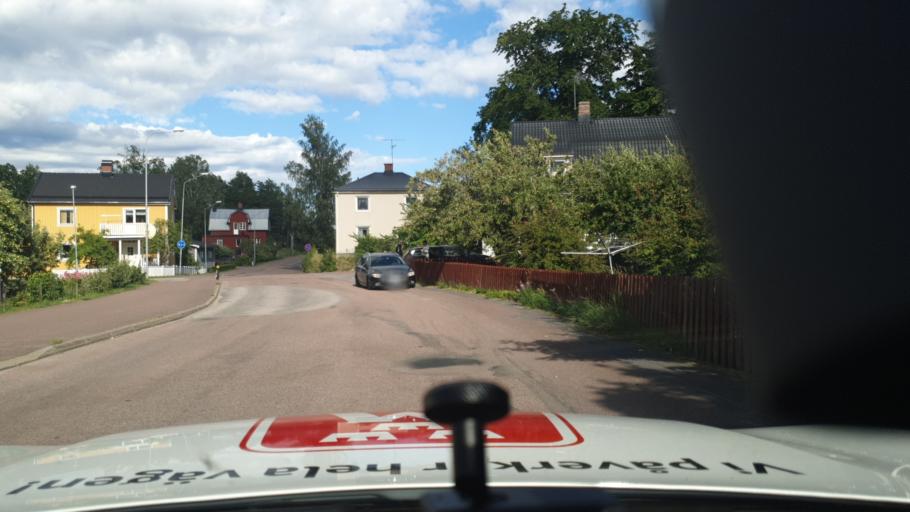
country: SE
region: Vaermland
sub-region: Saffle Kommun
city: Saeffle
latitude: 59.1386
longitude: 12.9288
